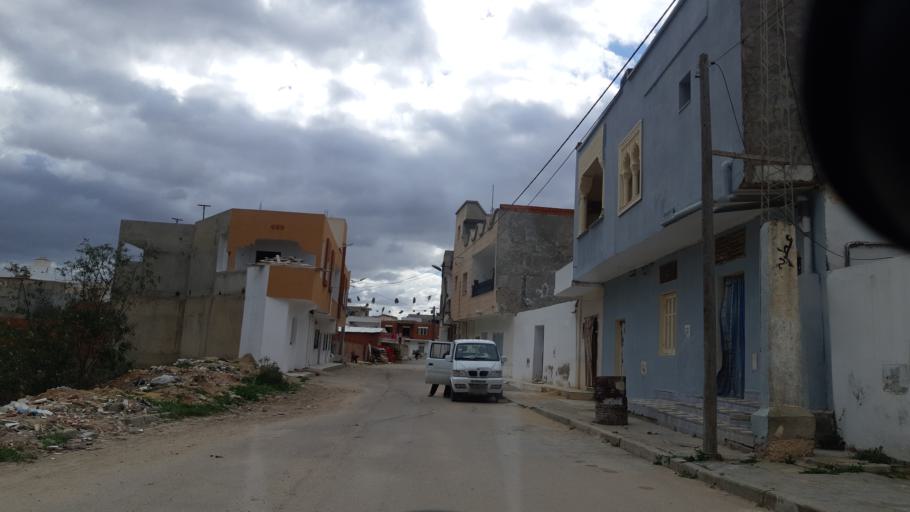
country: TN
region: Susah
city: Akouda
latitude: 35.8709
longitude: 10.5213
